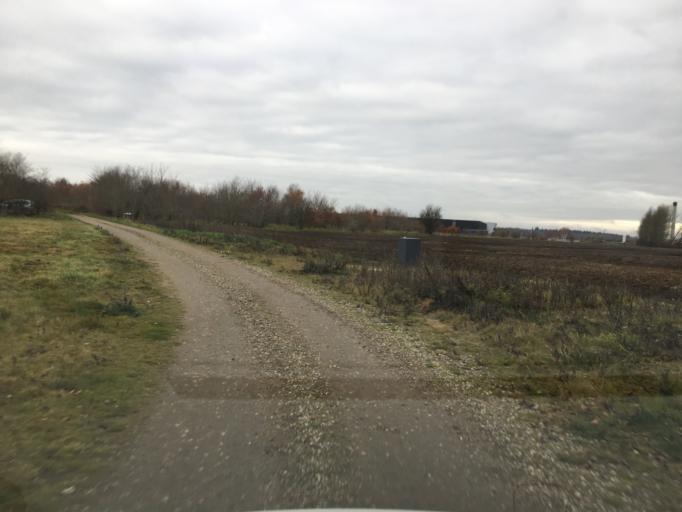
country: DK
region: South Denmark
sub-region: Tonder Kommune
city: Tonder
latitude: 54.9474
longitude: 8.8605
